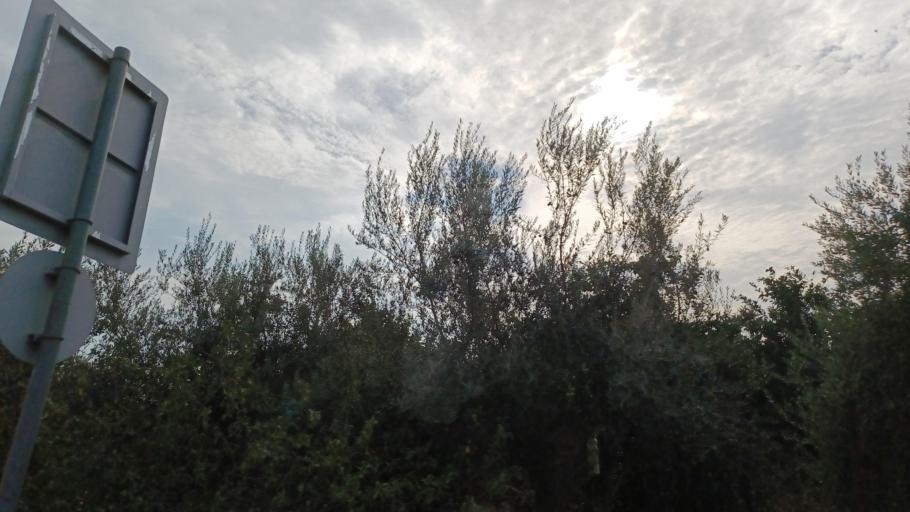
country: CY
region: Lefkosia
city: Peristerona
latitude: 35.1270
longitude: 33.0876
